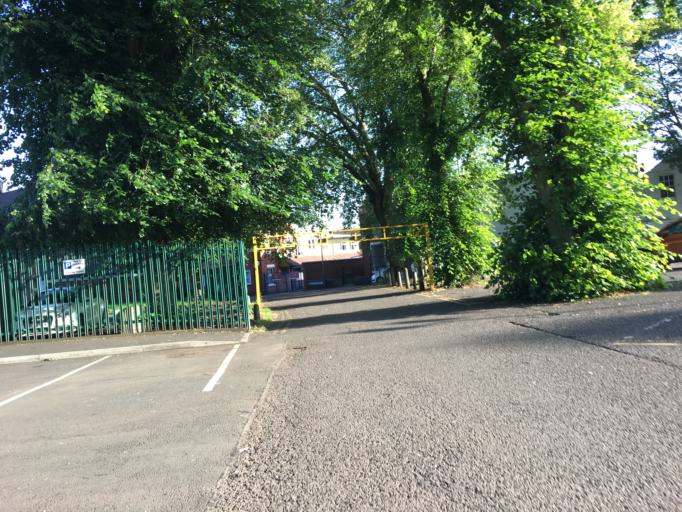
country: GB
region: England
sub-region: Warwickshire
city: Nuneaton
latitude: 52.5234
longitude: -1.4748
